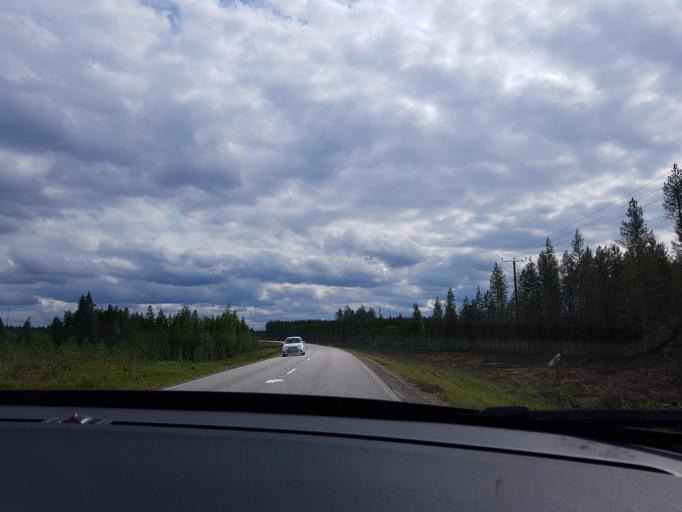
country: FI
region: Kainuu
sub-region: Kehys-Kainuu
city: Kuhmo
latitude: 64.3436
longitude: 29.8748
